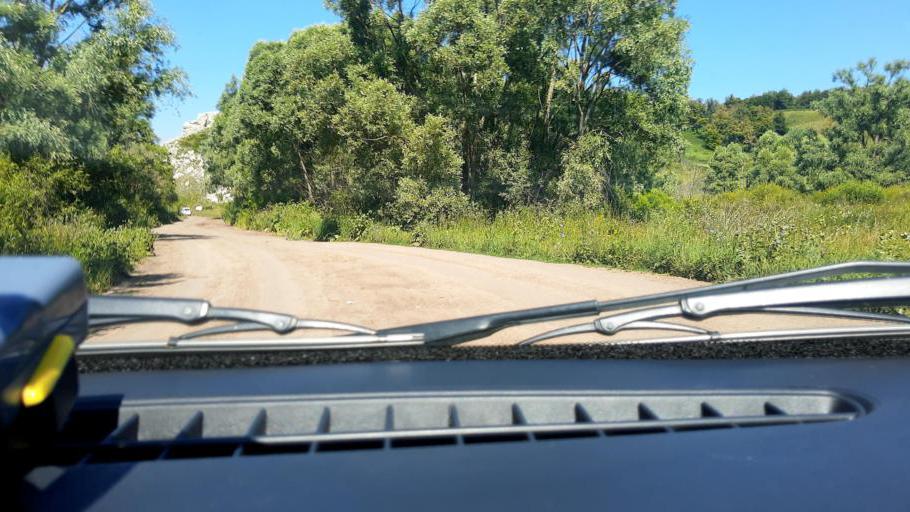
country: RU
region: Bashkortostan
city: Karmaskaly
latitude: 54.3585
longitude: 55.9030
